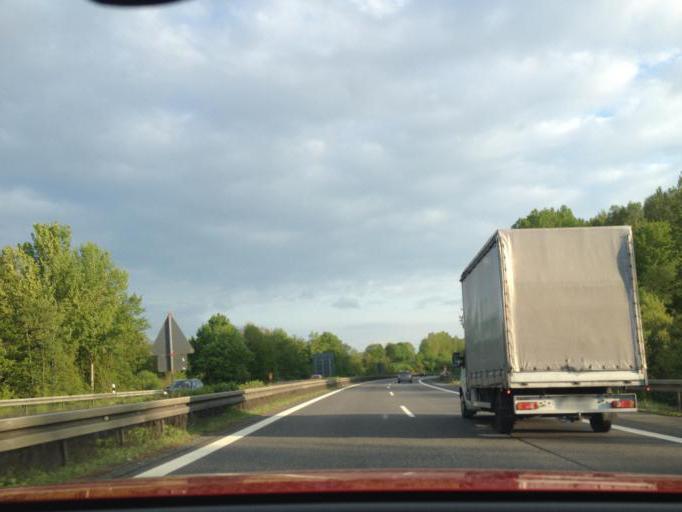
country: DE
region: Bavaria
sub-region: Upper Palatinate
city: Neustadt an der Waldnaab
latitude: 49.7327
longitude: 12.1569
